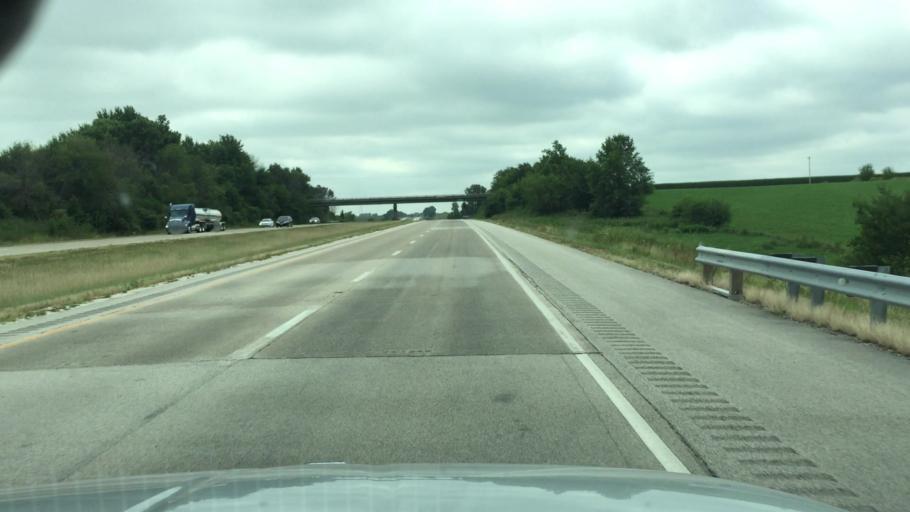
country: US
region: Illinois
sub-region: Henry County
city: Orion
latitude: 41.3271
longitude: -90.3349
